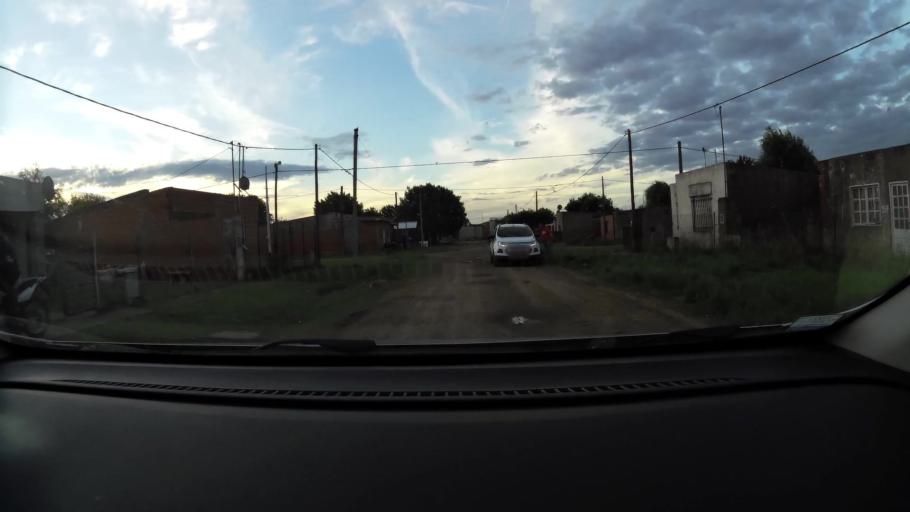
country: AR
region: Buenos Aires
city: San Nicolas de los Arroyos
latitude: -33.3169
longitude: -60.2475
